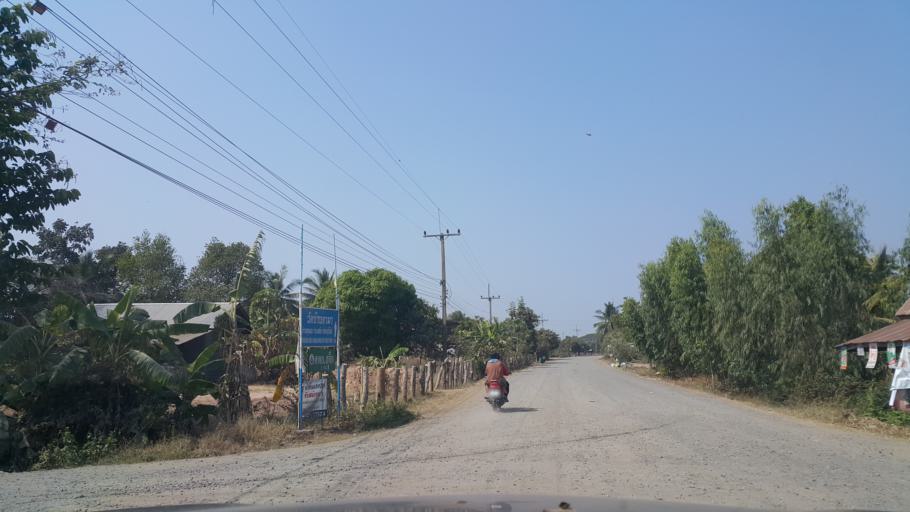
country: TH
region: Buriram
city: Ban Dan
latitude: 15.1324
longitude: 103.3475
